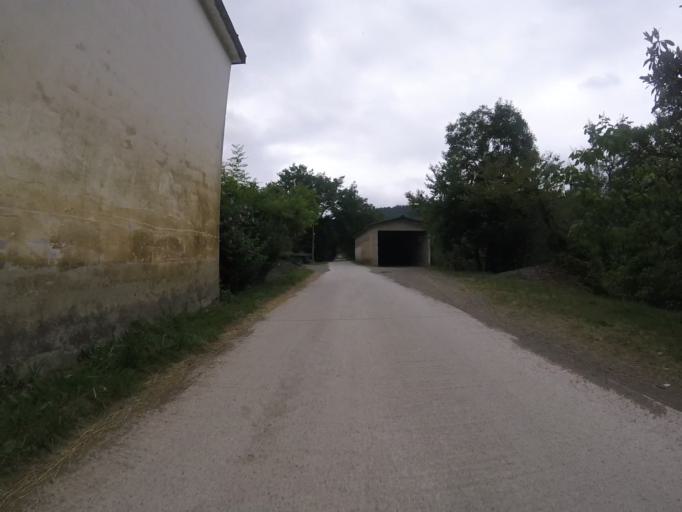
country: ES
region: Navarre
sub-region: Provincia de Navarra
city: Sunbilla
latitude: 43.1606
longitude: -1.6716
